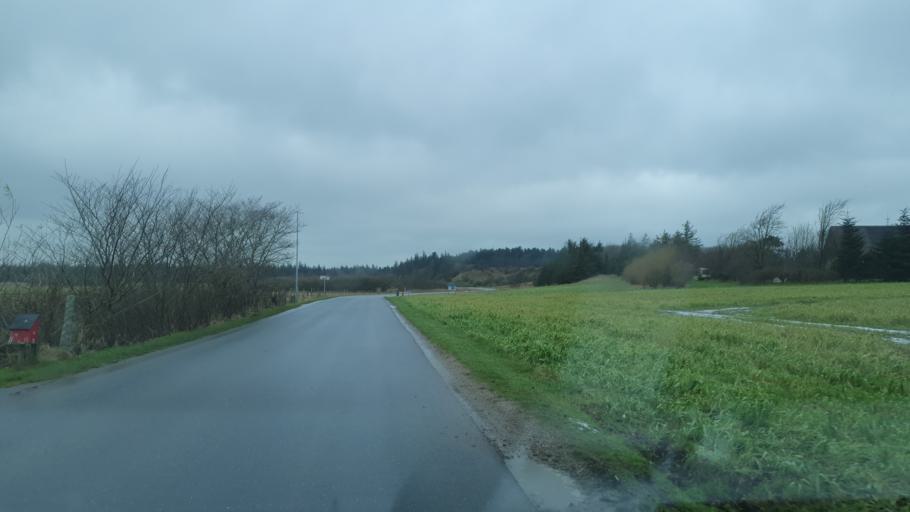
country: DK
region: North Denmark
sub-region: Jammerbugt Kommune
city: Fjerritslev
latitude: 57.1113
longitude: 9.1282
